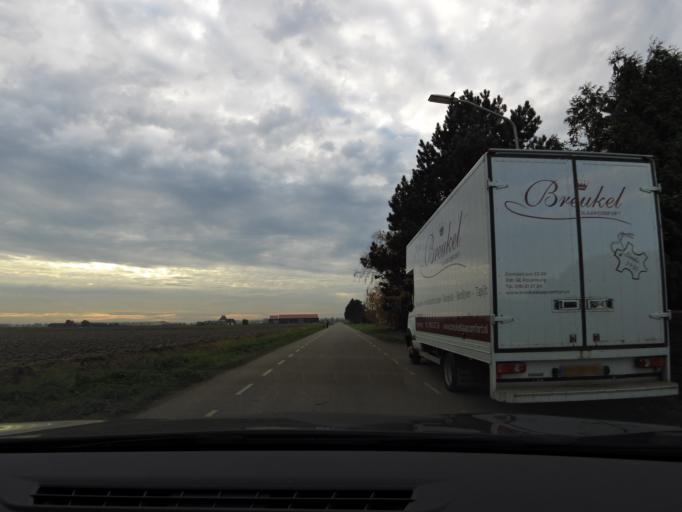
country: NL
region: South Holland
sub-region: Gemeente Goeree-Overflakkee
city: Dirksland
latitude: 51.7496
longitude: 4.0875
